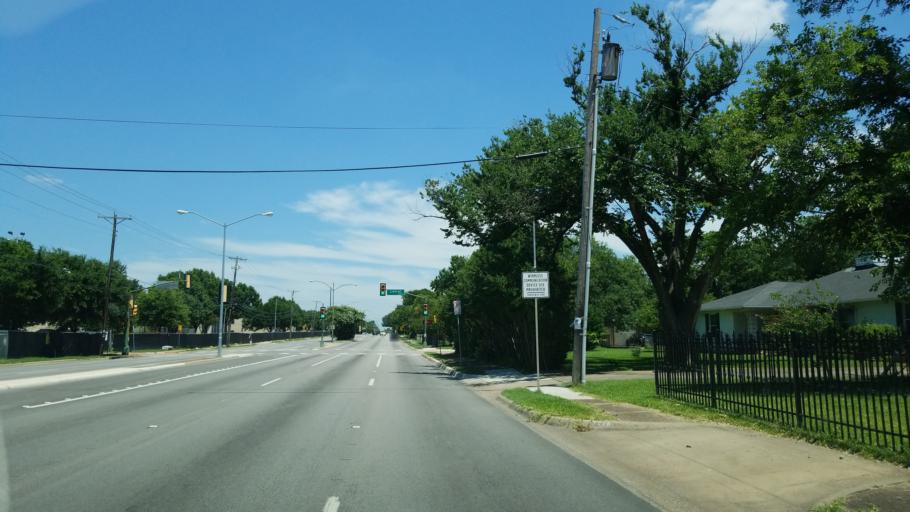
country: US
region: Texas
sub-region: Dallas County
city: University Park
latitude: 32.8803
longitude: -96.8470
